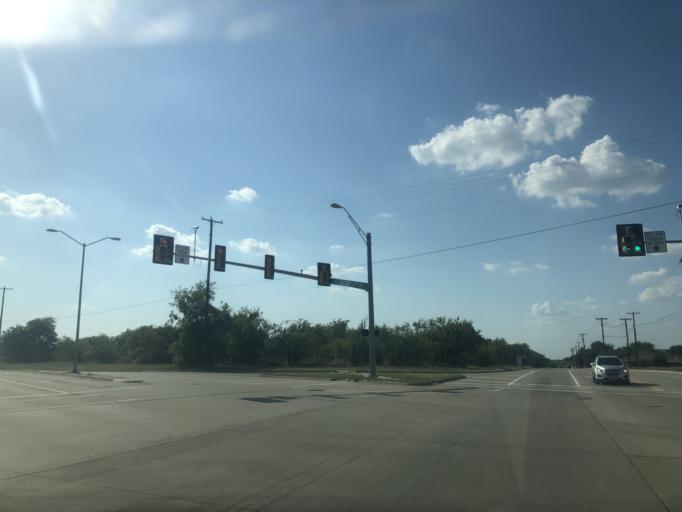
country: US
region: Texas
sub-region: Tarrant County
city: Saginaw
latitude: 32.8479
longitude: -97.3863
